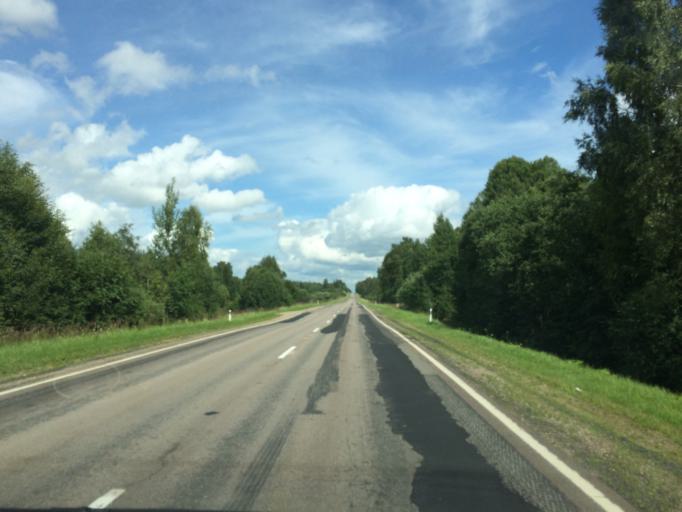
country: LV
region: Rezekne
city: Rezekne
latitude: 56.6461
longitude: 27.4895
